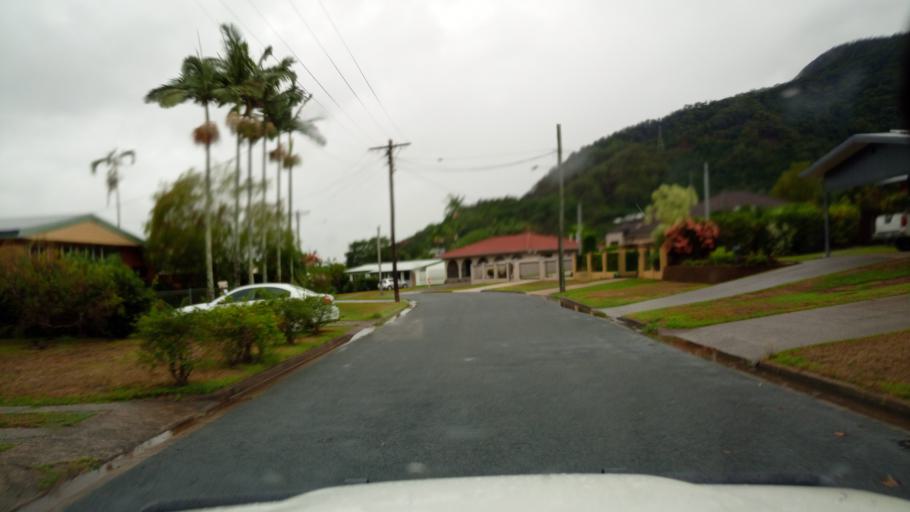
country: AU
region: Queensland
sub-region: Cairns
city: Woree
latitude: -16.9597
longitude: 145.7284
